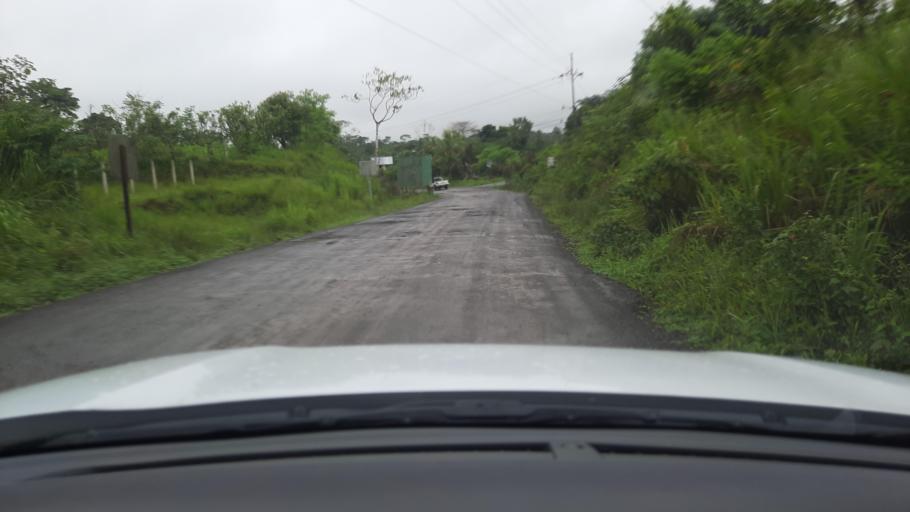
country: CR
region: Alajuela
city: San Jose
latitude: 11.0125
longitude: -85.3502
